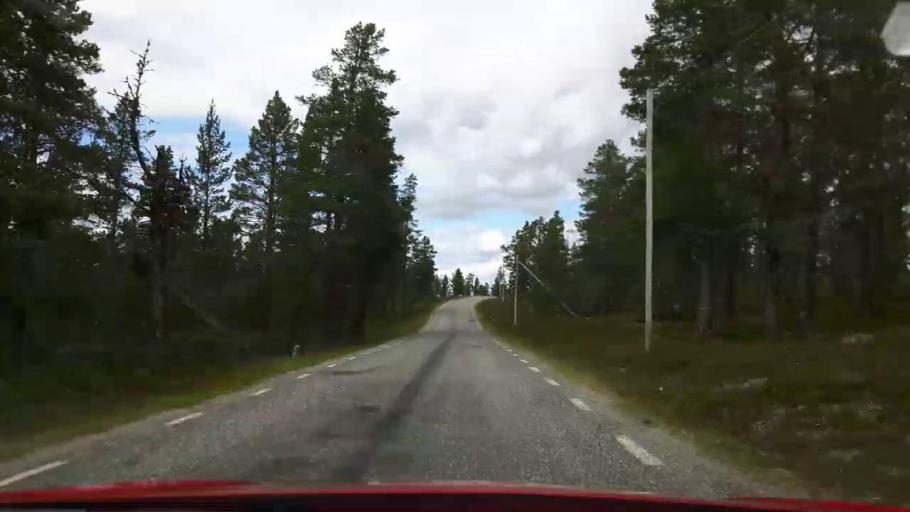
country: NO
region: Hedmark
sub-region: Engerdal
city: Engerdal
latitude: 62.3144
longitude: 12.8093
